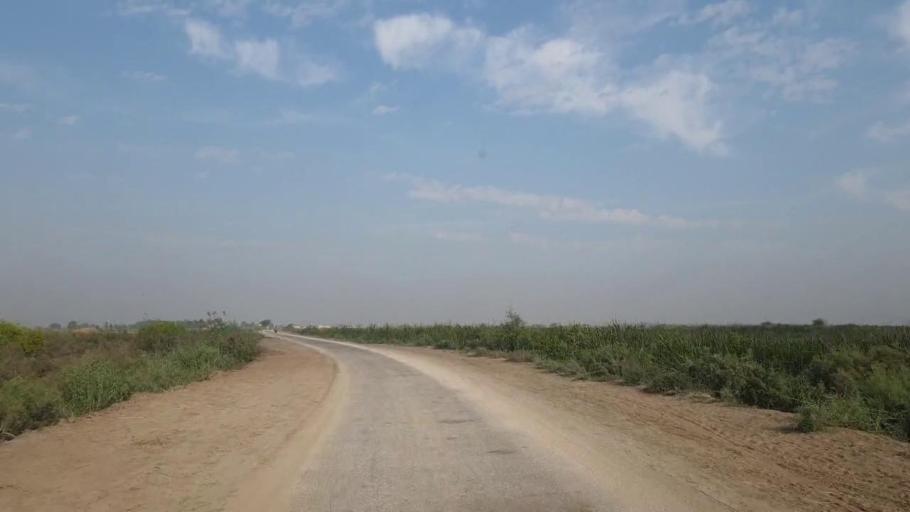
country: PK
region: Sindh
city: Tando Bago
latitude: 24.8507
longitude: 68.9712
